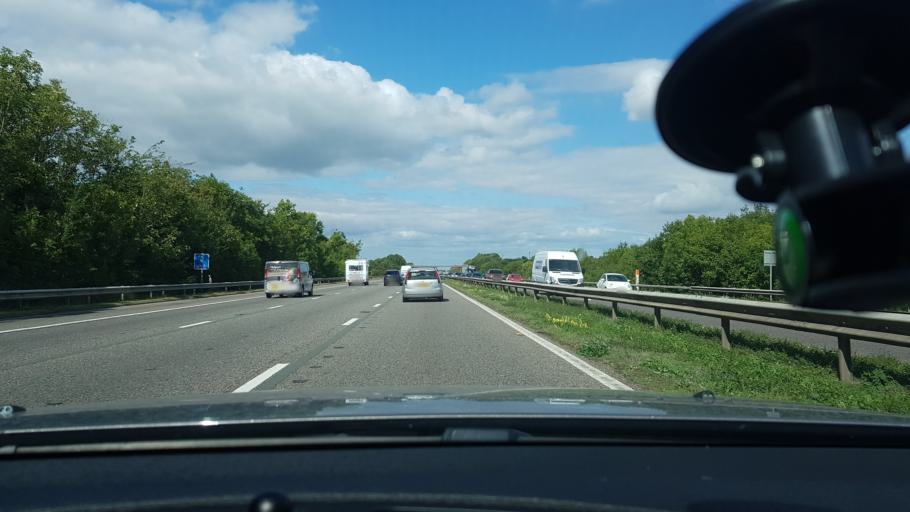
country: GB
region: England
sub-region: North Somerset
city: Banwell
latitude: 51.3342
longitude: -2.8937
